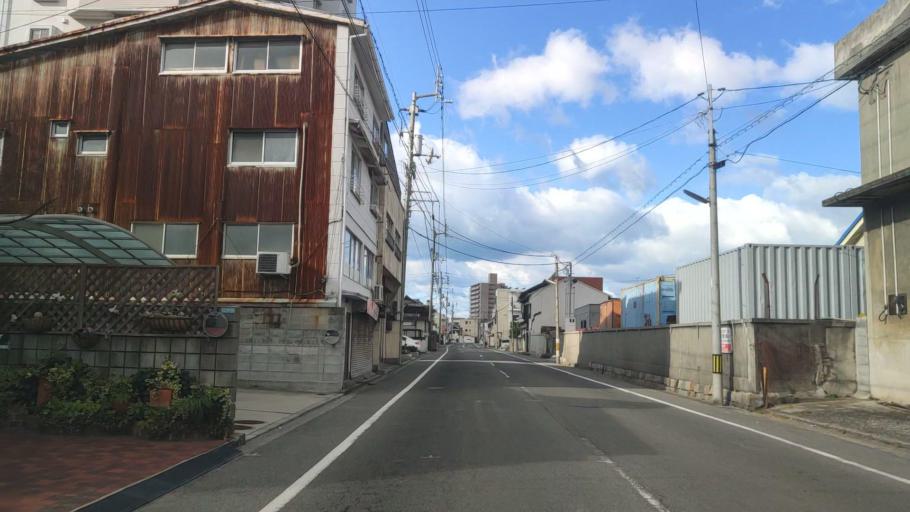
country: JP
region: Ehime
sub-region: Shikoku-chuo Shi
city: Matsuyama
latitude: 33.8644
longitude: 132.7185
